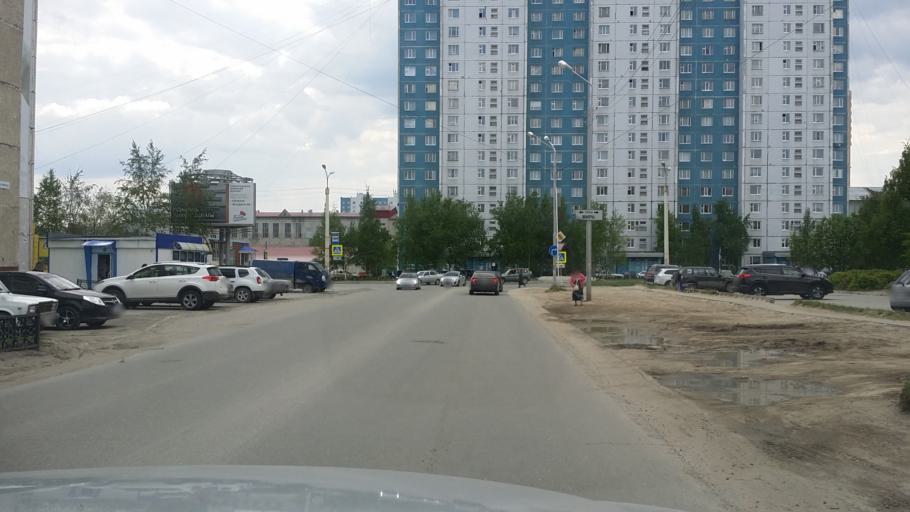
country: RU
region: Khanty-Mansiyskiy Avtonomnyy Okrug
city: Nizhnevartovsk
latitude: 60.9366
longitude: 76.6071
